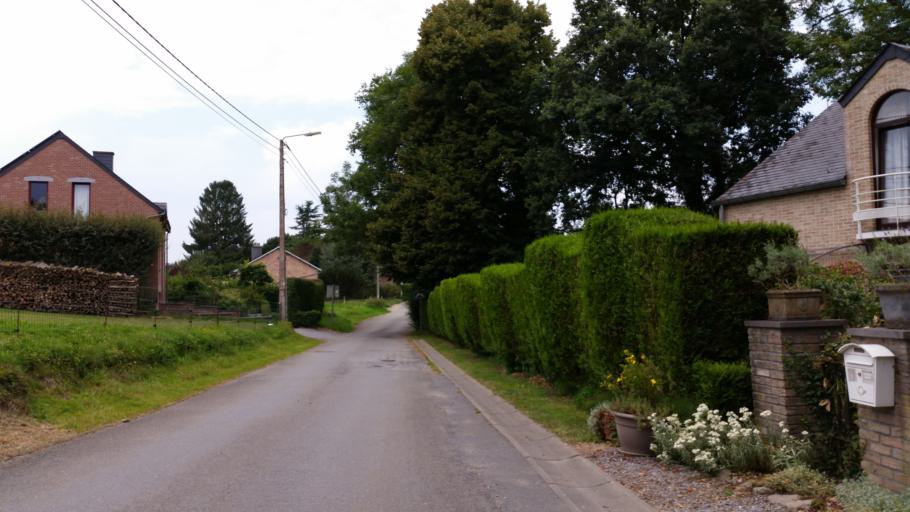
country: BE
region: Wallonia
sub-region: Province du Luxembourg
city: Durbuy
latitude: 50.3506
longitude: 5.4585
